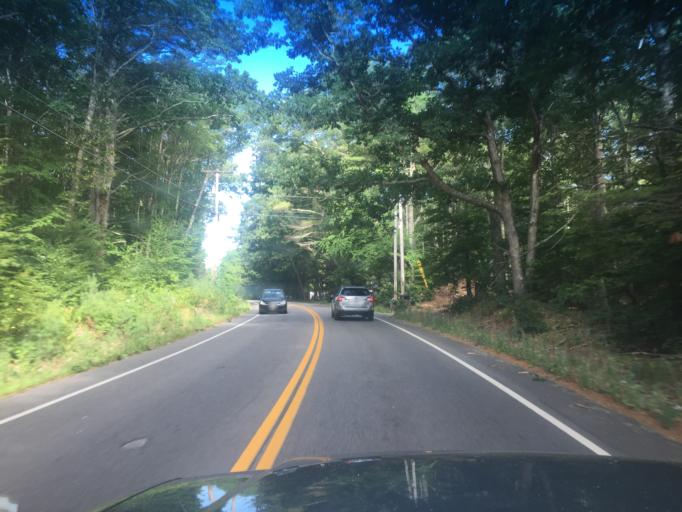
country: US
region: Maine
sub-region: York County
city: South Berwick
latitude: 43.2028
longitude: -70.7681
